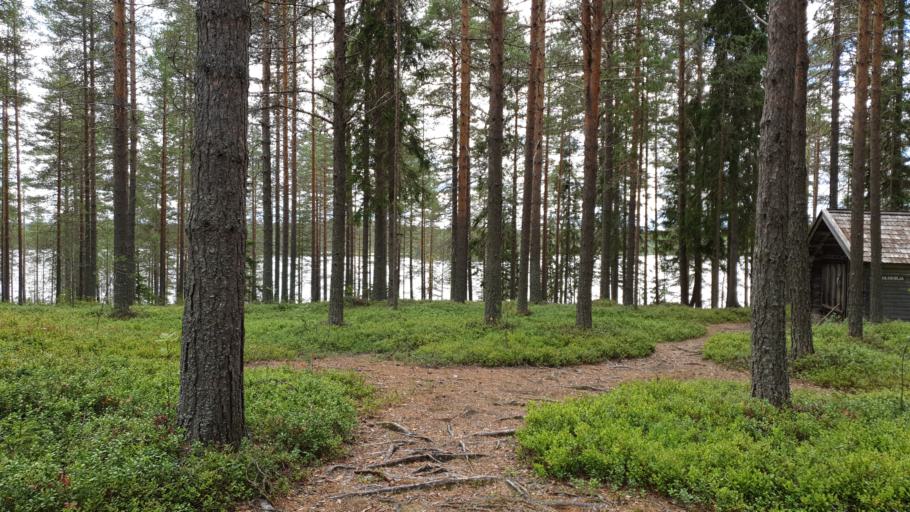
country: FI
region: Kainuu
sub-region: Kehys-Kainuu
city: Kuhmo
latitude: 64.3815
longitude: 29.8067
